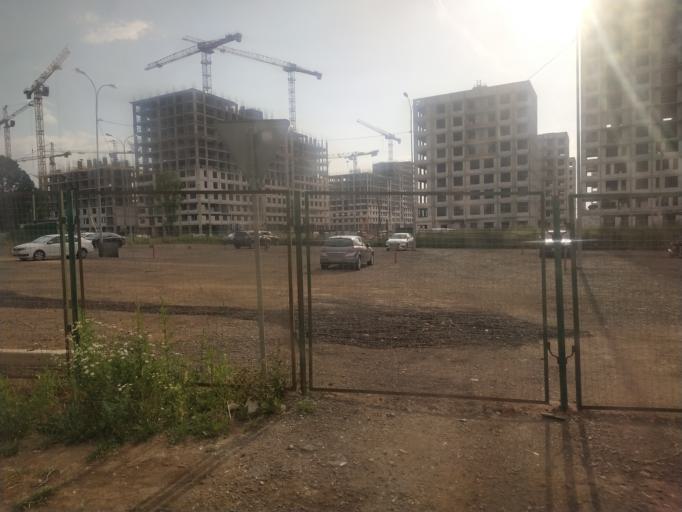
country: RU
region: Moskovskaya
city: Mosrentgen
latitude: 55.5910
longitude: 37.4500
